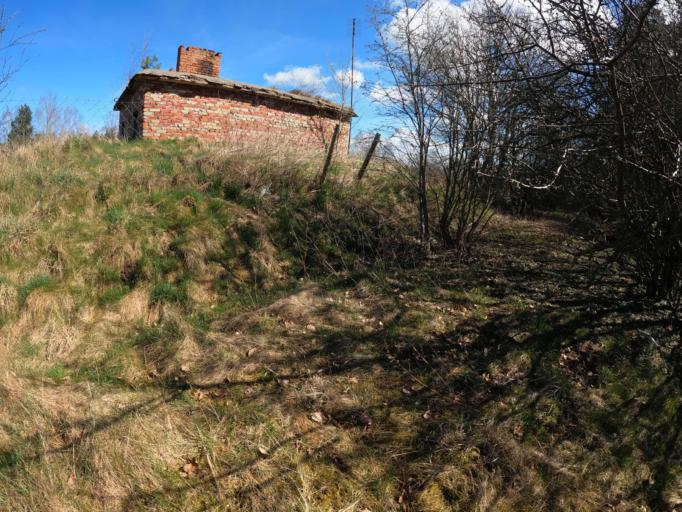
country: PL
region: West Pomeranian Voivodeship
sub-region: Powiat gryficki
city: Gryfice
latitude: 53.9252
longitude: 15.2250
